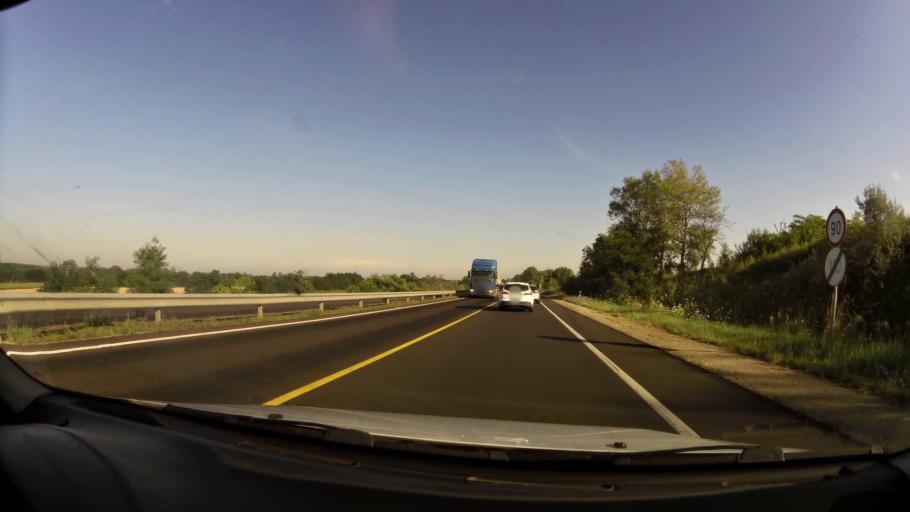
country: HU
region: Pest
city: Cegledbercel
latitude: 47.2401
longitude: 19.6598
